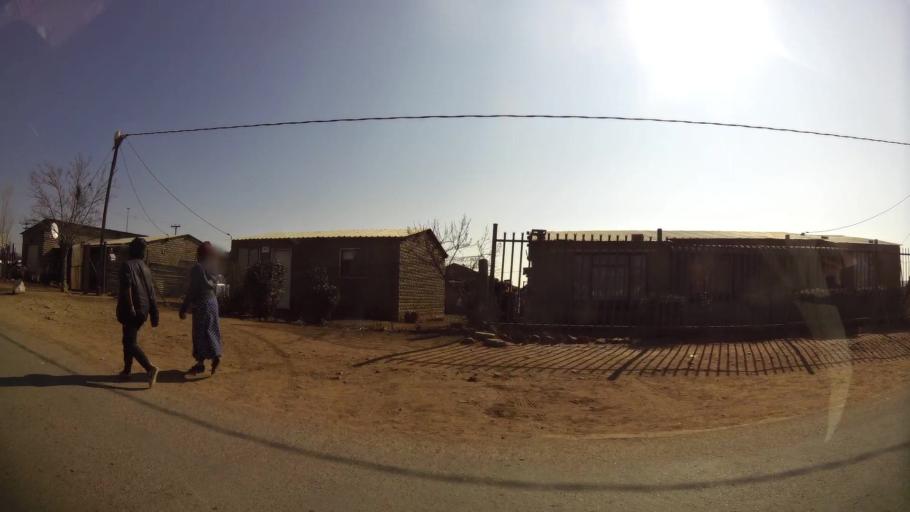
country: ZA
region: Orange Free State
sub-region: Mangaung Metropolitan Municipality
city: Bloemfontein
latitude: -29.2009
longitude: 26.2502
